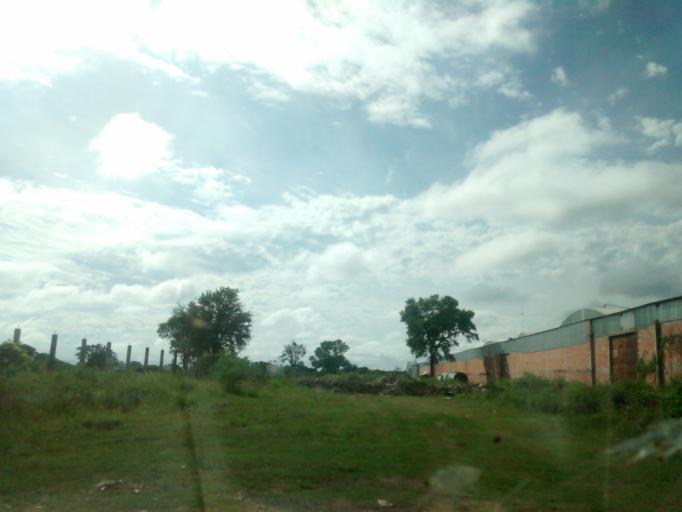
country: AR
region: Chaco
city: Fontana
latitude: -27.4080
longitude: -58.9778
